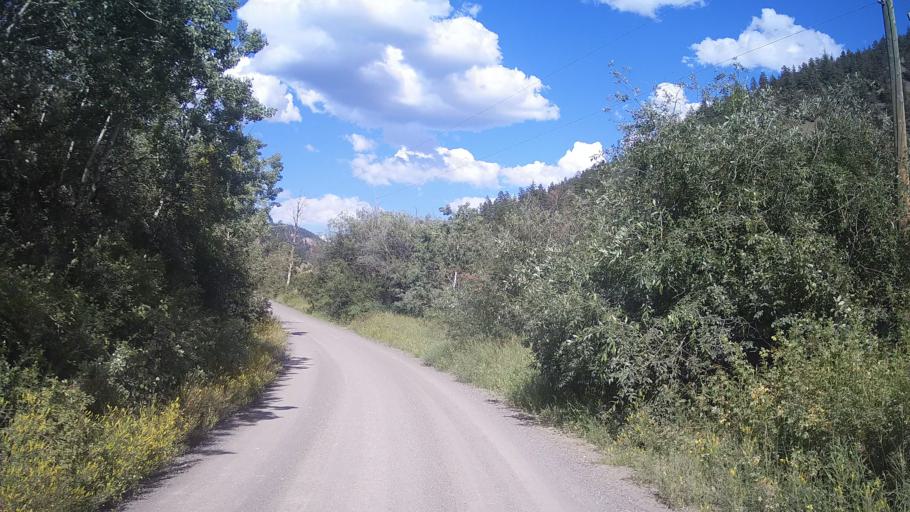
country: CA
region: British Columbia
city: Lillooet
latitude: 51.2422
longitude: -122.0403
